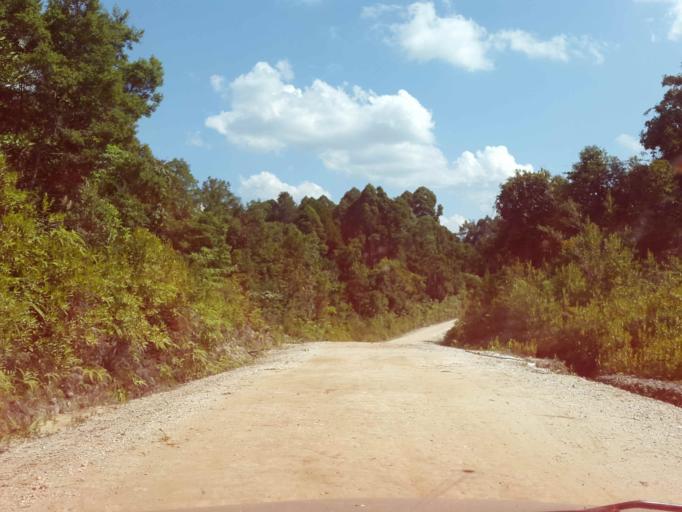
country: MY
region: Sarawak
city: Simanggang
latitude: 0.7308
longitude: 111.5672
